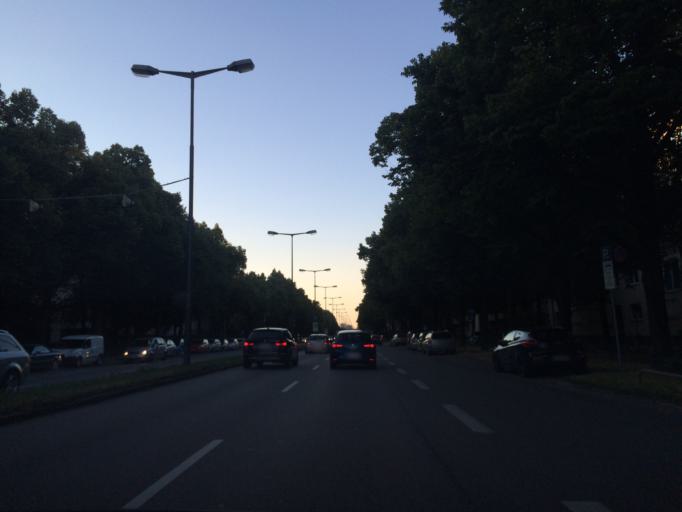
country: DE
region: Bavaria
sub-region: Upper Bavaria
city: Munich
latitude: 48.1570
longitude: 11.5373
